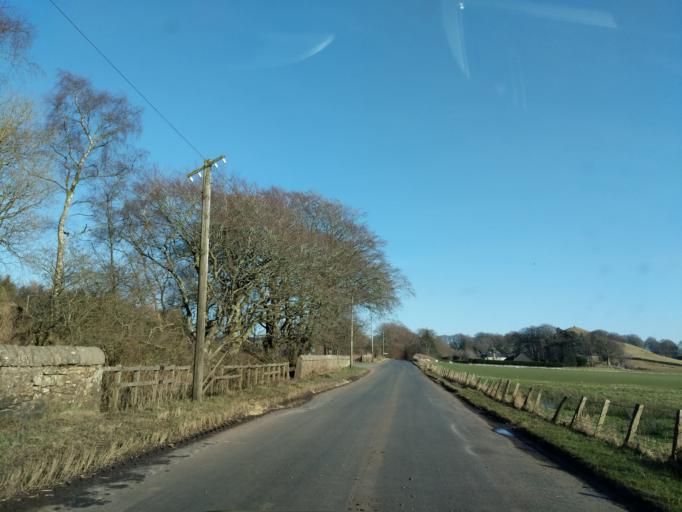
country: GB
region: Scotland
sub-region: The Scottish Borders
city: West Linton
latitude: 55.7179
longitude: -3.4237
